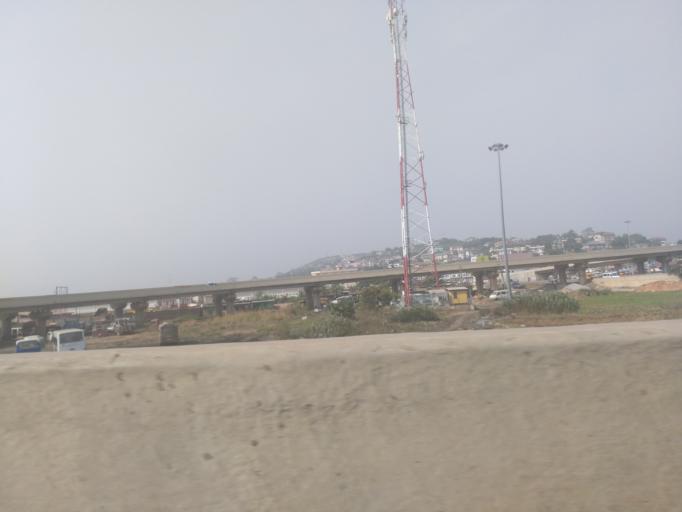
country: GH
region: Greater Accra
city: Gbawe
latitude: 5.5707
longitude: -0.2821
